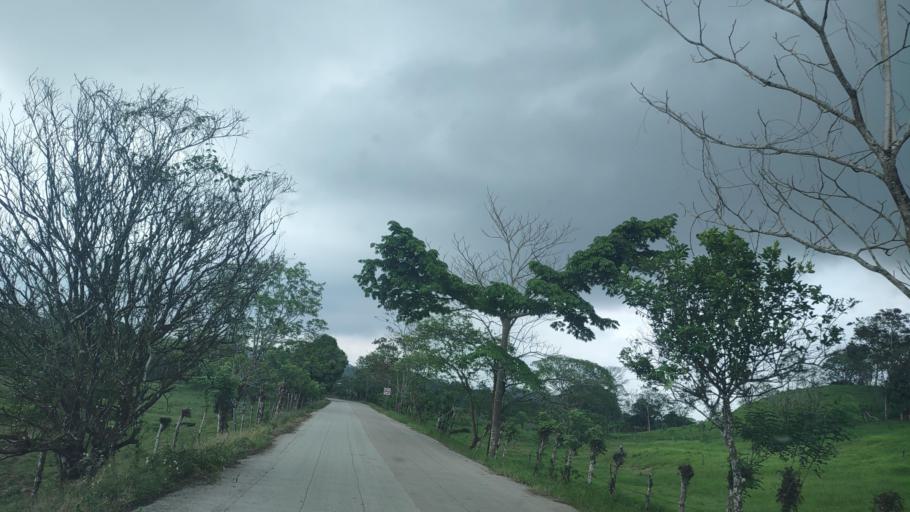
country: MX
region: Veracruz
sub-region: Uxpanapa
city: Poblado 10
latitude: 17.4943
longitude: -94.1691
